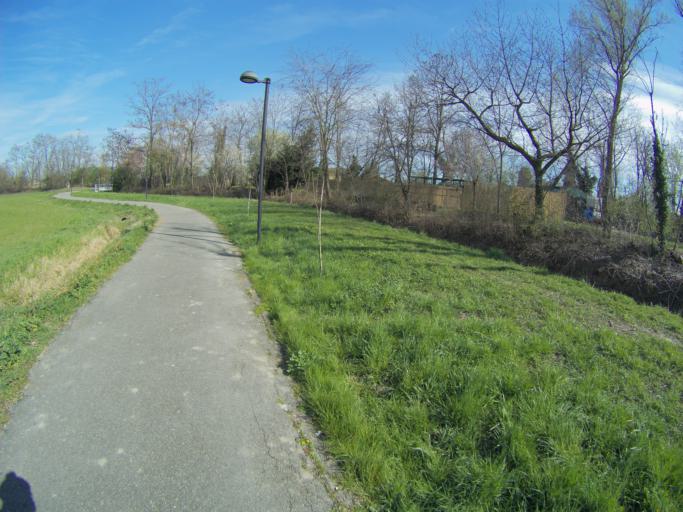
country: IT
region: Emilia-Romagna
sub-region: Provincia di Reggio Emilia
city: Massenzatico
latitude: 44.7020
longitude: 10.6738
